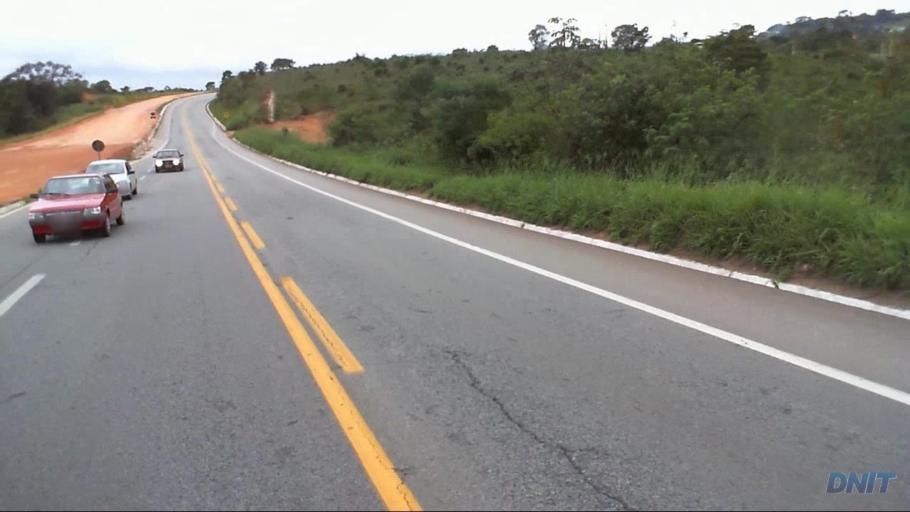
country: BR
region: Minas Gerais
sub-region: Barao De Cocais
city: Barao de Cocais
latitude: -19.7593
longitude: -43.4658
